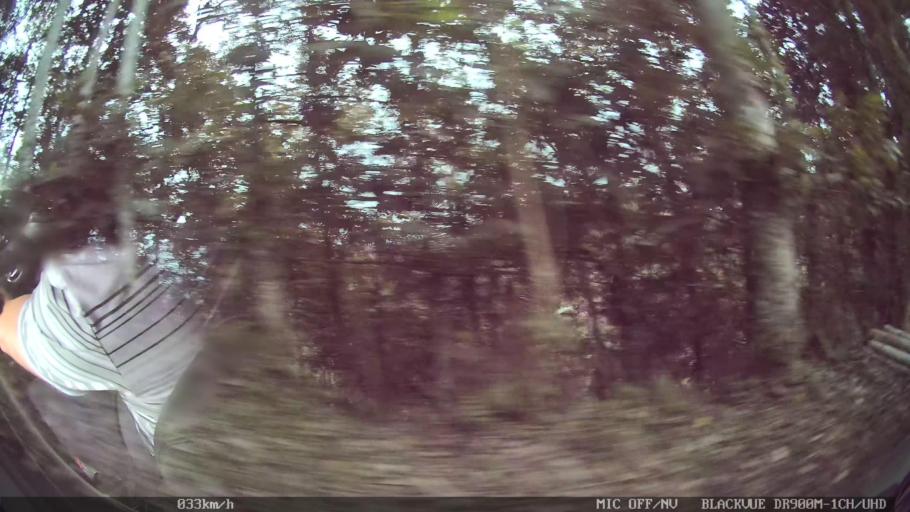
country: ID
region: Bali
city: Peneng
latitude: -8.3595
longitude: 115.2064
